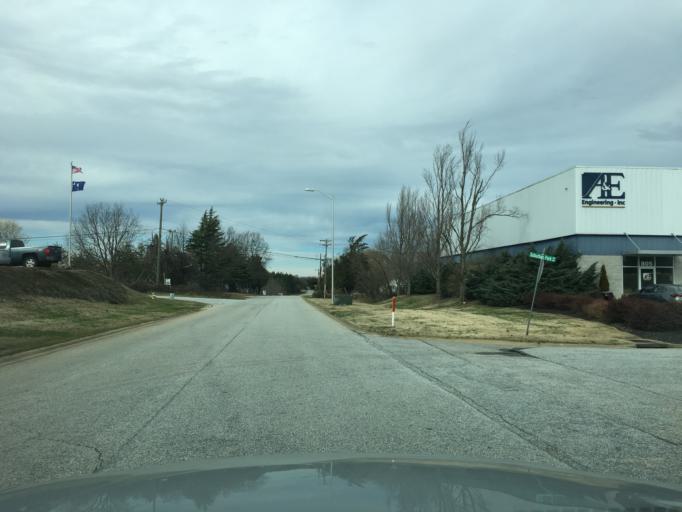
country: US
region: South Carolina
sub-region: Spartanburg County
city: Duncan
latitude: 34.9104
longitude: -82.1854
